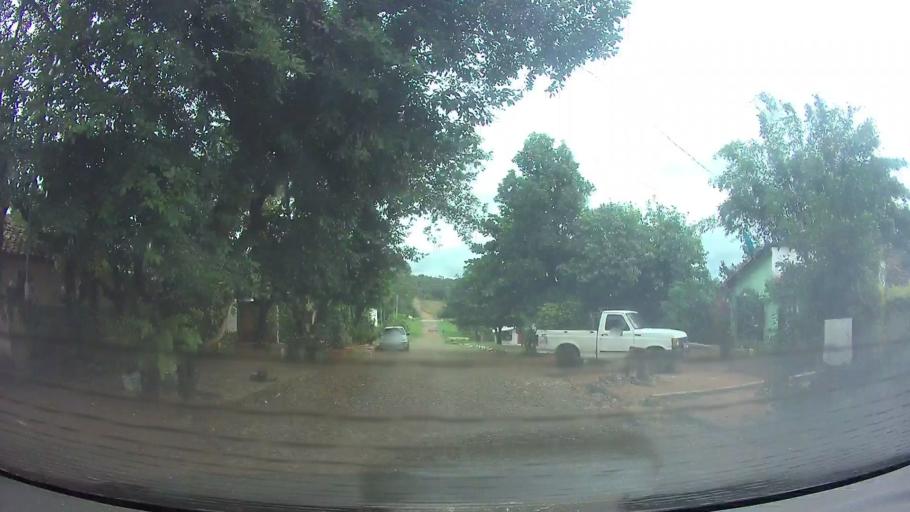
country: PY
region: Cordillera
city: Atyra
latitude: -25.2828
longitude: -57.1735
